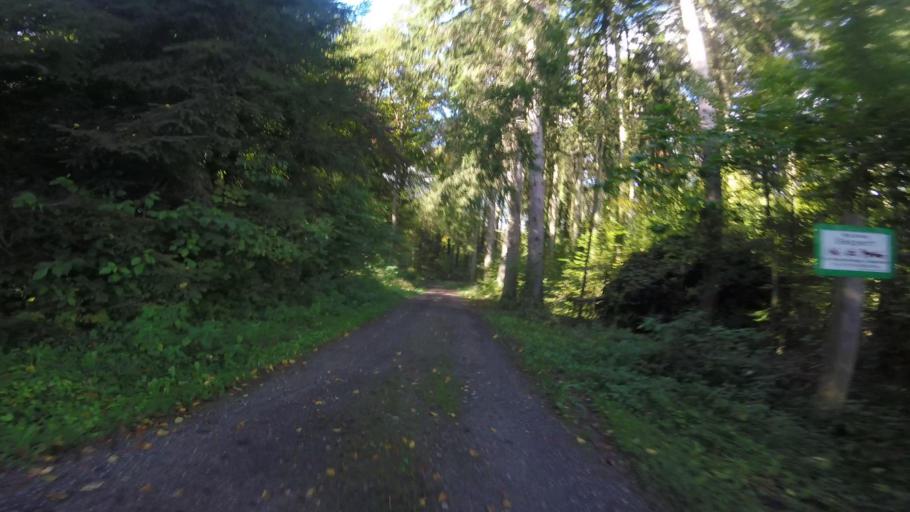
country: DE
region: Baden-Wuerttemberg
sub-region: Regierungsbezirk Stuttgart
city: Aspach
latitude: 48.9804
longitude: 9.3917
